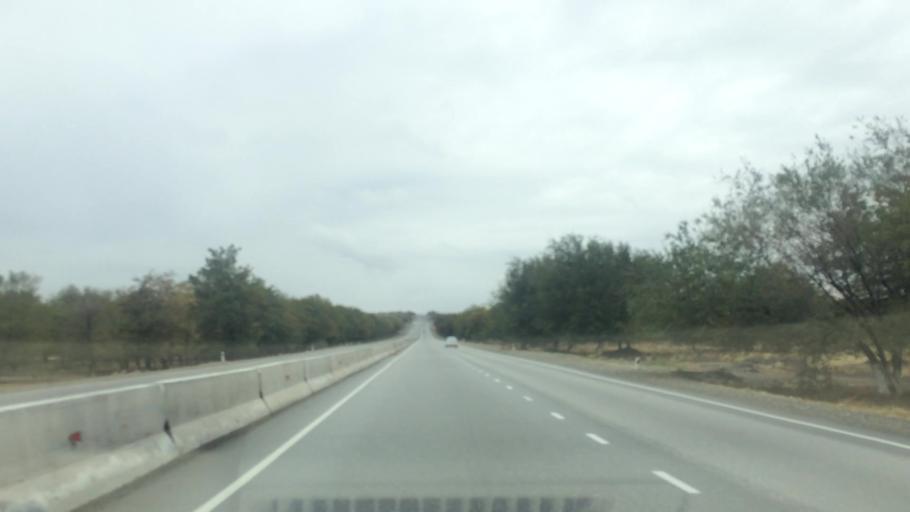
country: UZ
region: Samarqand
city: Bulung'ur
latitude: 39.8732
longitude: 67.4799
